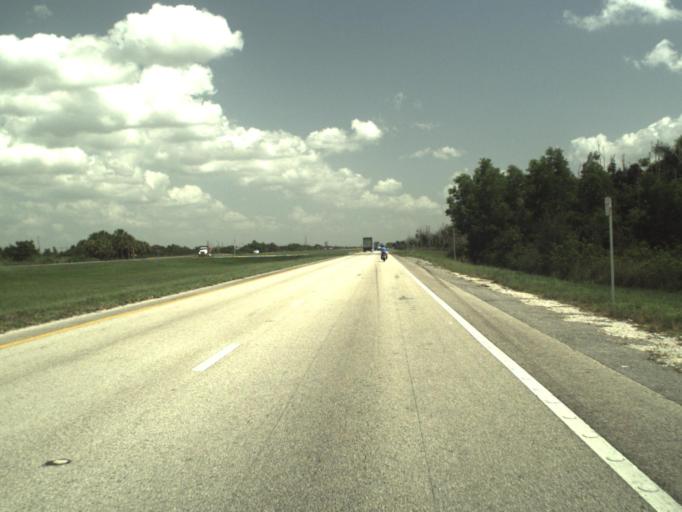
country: US
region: Florida
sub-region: Broward County
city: Weston
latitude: 26.0643
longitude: -80.4336
